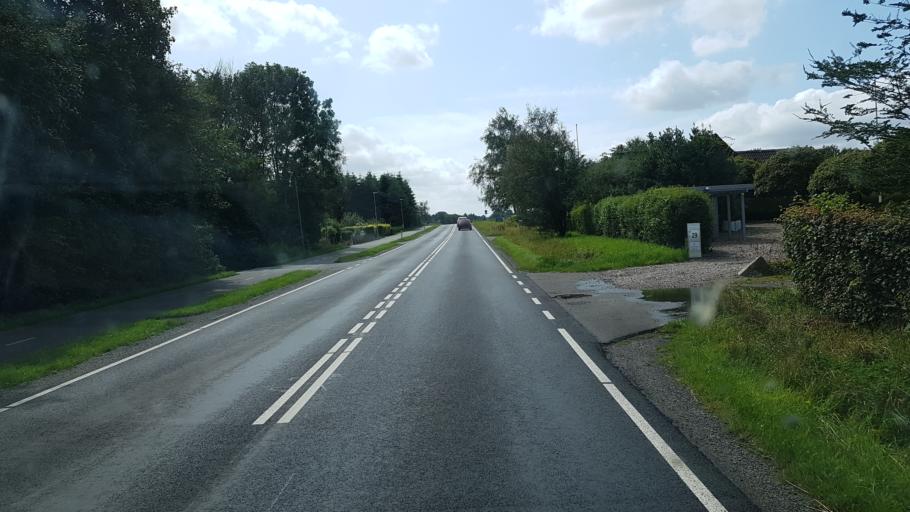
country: DK
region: South Denmark
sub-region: Vejen Kommune
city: Vejen
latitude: 55.5626
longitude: 9.1291
